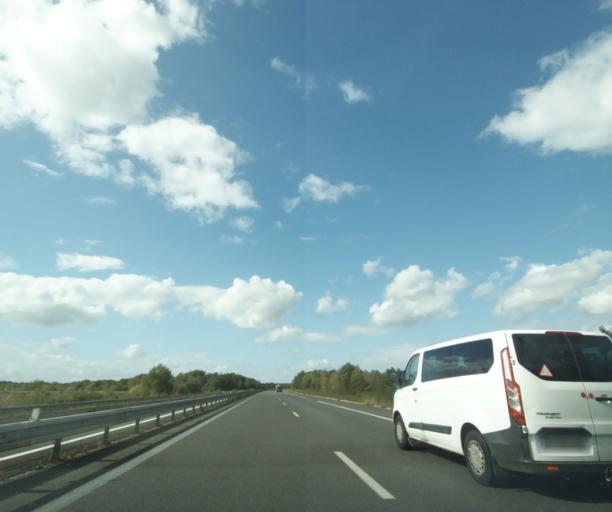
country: FR
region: Centre
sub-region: Departement du Loiret
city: Jouy-le-Potier
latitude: 47.7387
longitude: 1.8707
